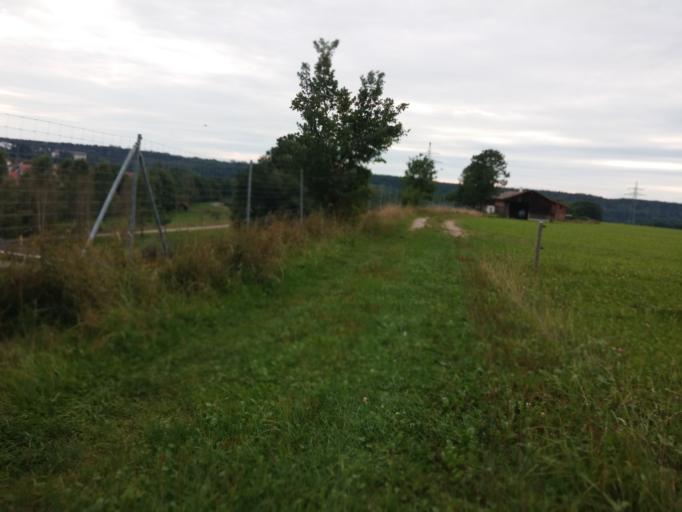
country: DE
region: Bavaria
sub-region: Swabia
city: Lautrach
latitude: 47.9050
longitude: 10.1331
